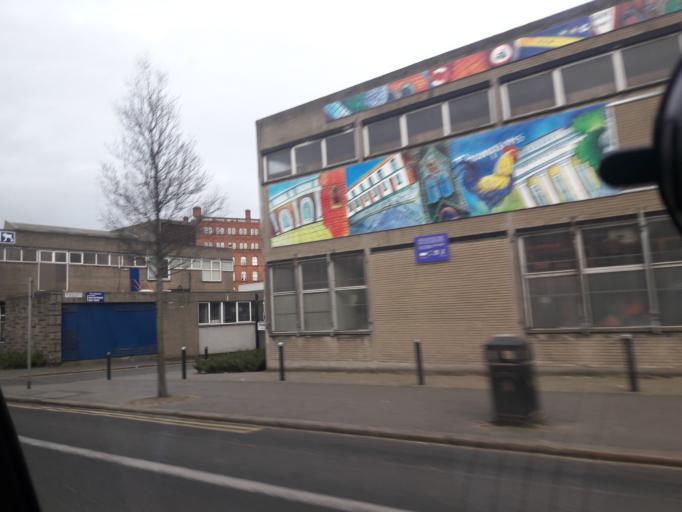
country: GB
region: Northern Ireland
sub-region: City of Belfast
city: Belfast
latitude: 54.6153
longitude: -5.9243
